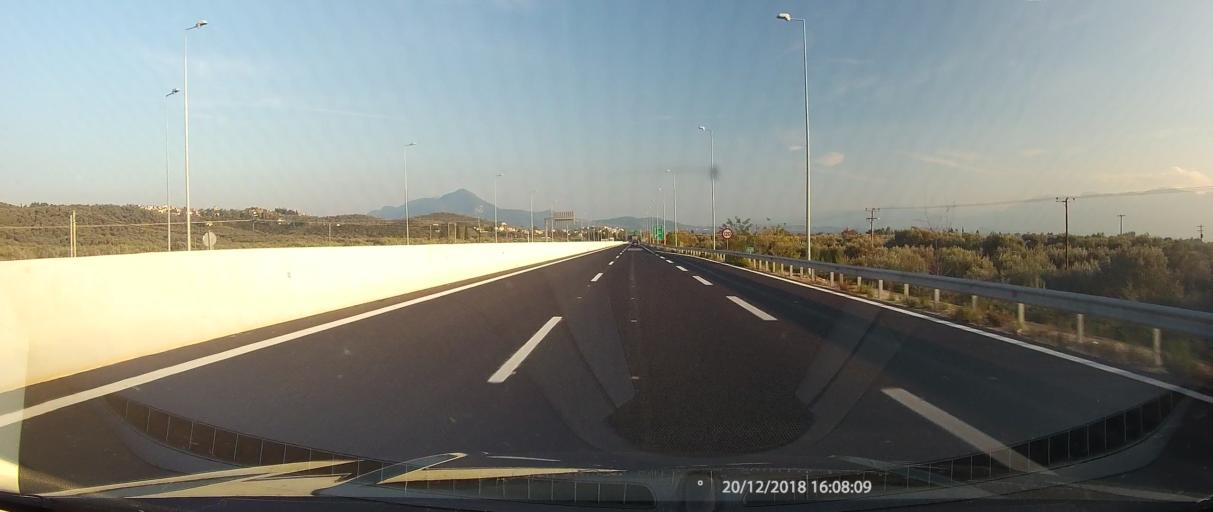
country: GR
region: Central Greece
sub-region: Nomos Fthiotidos
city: Pelasgia
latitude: 38.8887
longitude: 22.7584
